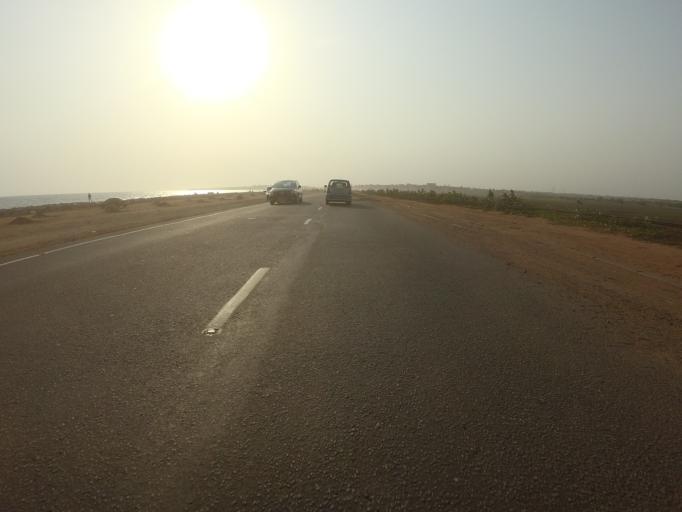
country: GH
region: Greater Accra
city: Nungua
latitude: 5.6133
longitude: -0.0354
